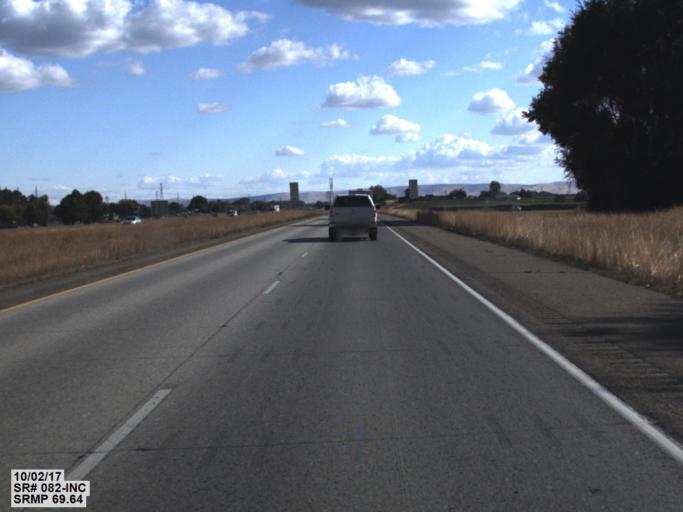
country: US
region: Washington
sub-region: Yakima County
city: Sunnyside
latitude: 46.3021
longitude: -119.9664
